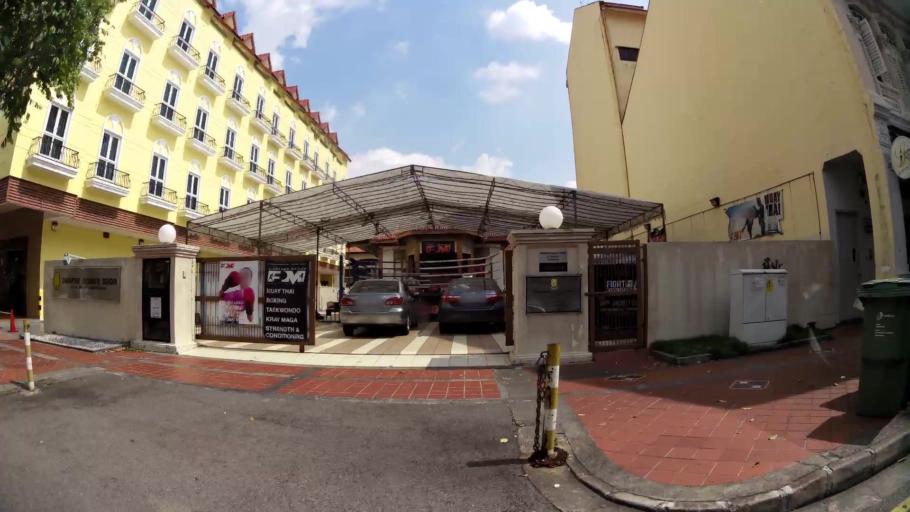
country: SG
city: Singapore
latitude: 1.3112
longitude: 103.9011
